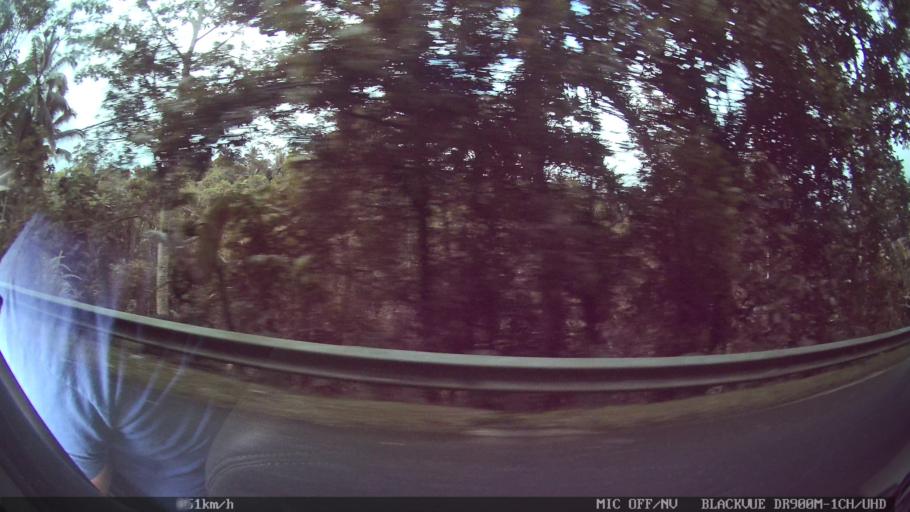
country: ID
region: Bali
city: Petang
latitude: -8.3892
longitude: 115.2199
